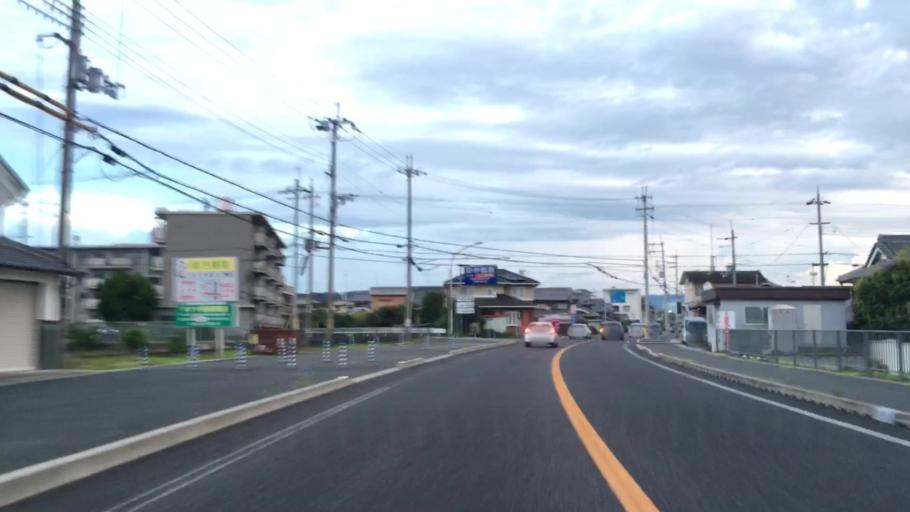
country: JP
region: Hyogo
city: Himeji
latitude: 34.9122
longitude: 134.7391
